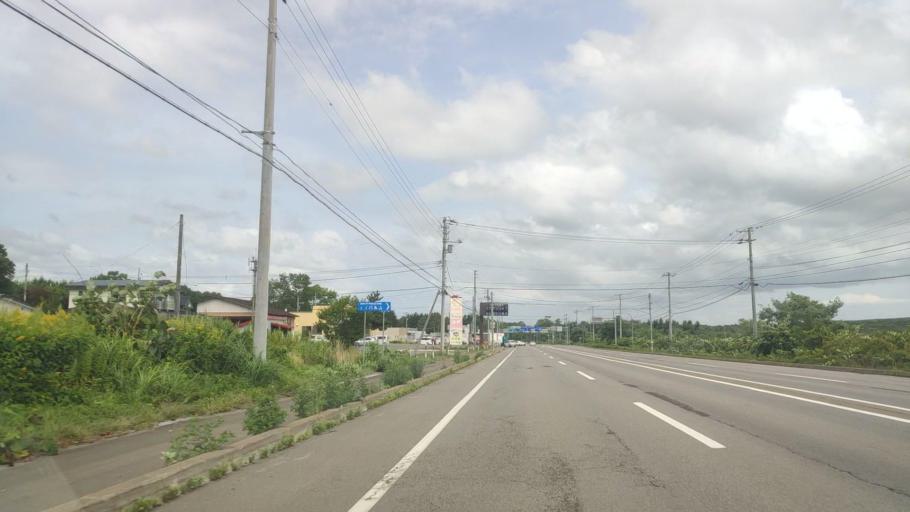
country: JP
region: Hokkaido
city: Nanae
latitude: 42.0047
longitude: 140.6327
